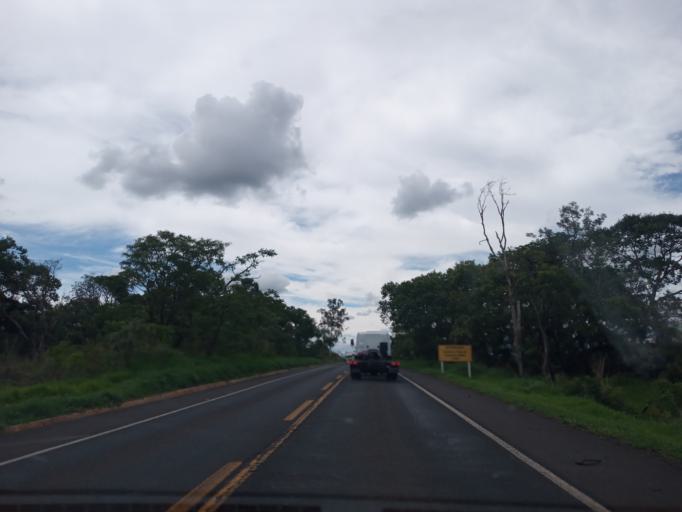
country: BR
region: Minas Gerais
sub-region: Uberlandia
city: Uberlandia
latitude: -19.1820
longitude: -47.8798
